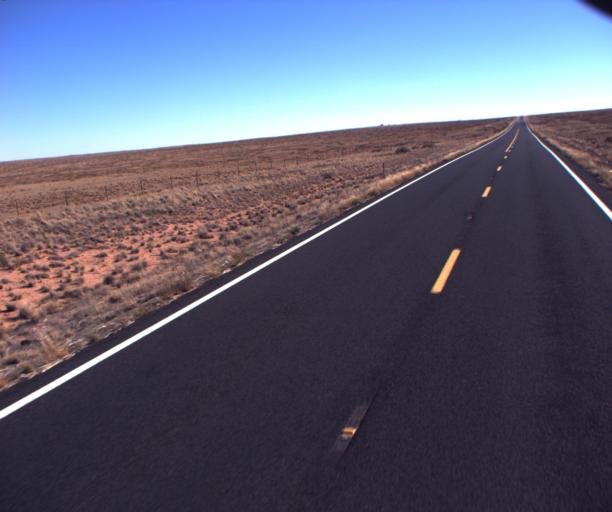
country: US
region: Arizona
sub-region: Coconino County
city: Tuba City
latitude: 36.0156
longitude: -111.0948
